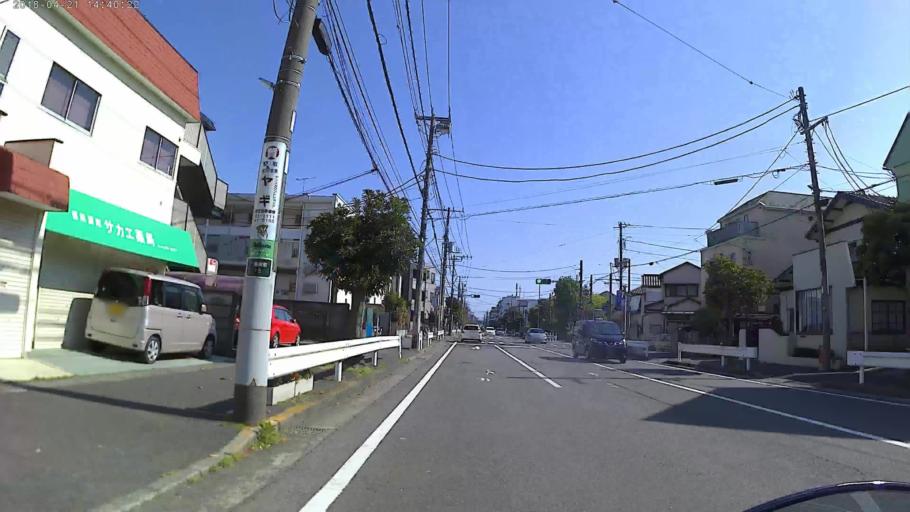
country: JP
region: Kanagawa
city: Hiratsuka
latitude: 35.3242
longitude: 139.3464
